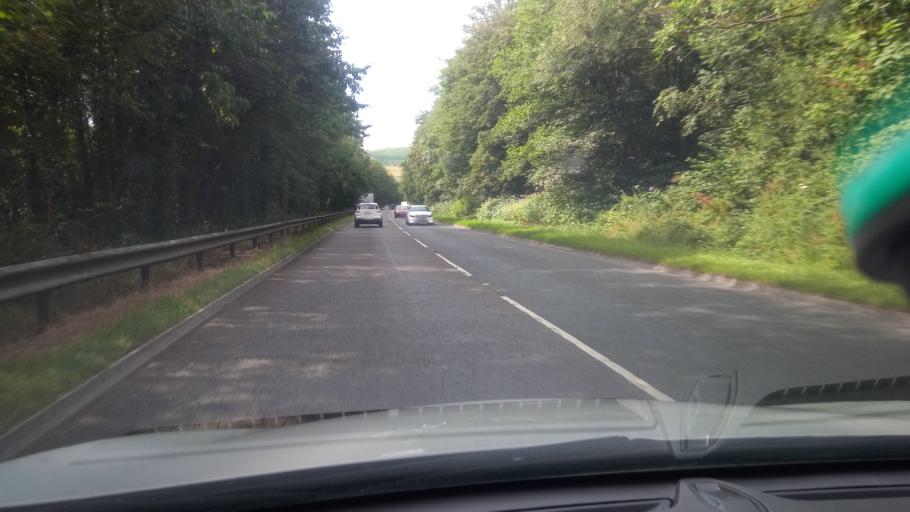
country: GB
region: Wales
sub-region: Rhondda Cynon Taf
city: Tonyrefail
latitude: 51.5804
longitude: -3.4327
